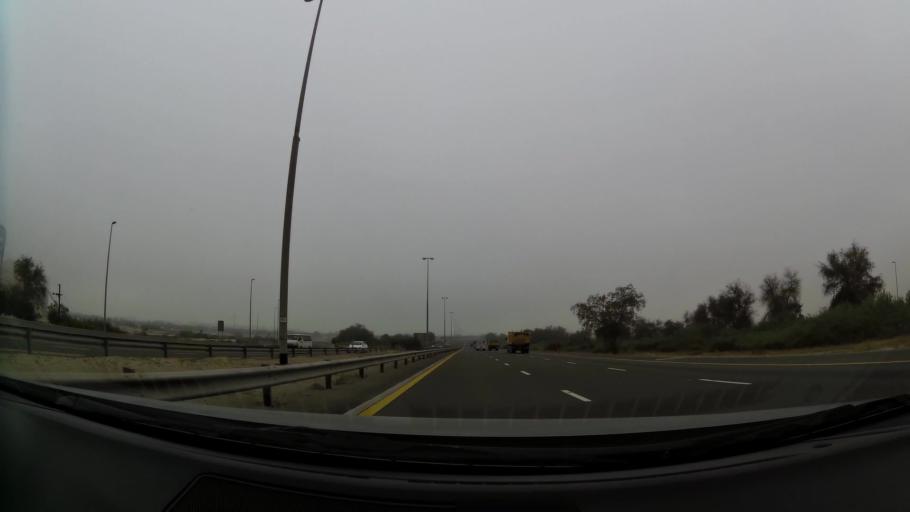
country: AE
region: Dubai
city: Dubai
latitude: 25.1068
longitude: 55.3759
